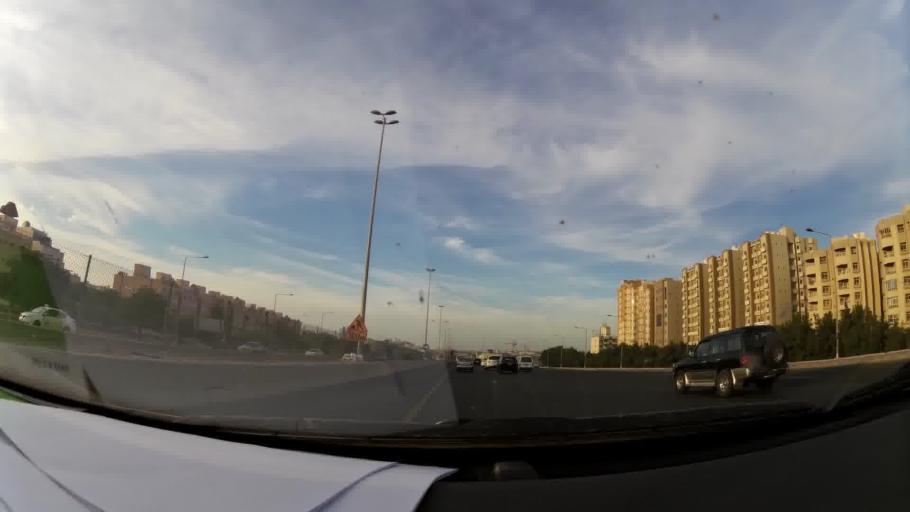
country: KW
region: Al Ahmadi
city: Al Fintas
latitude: 29.1797
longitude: 48.1134
